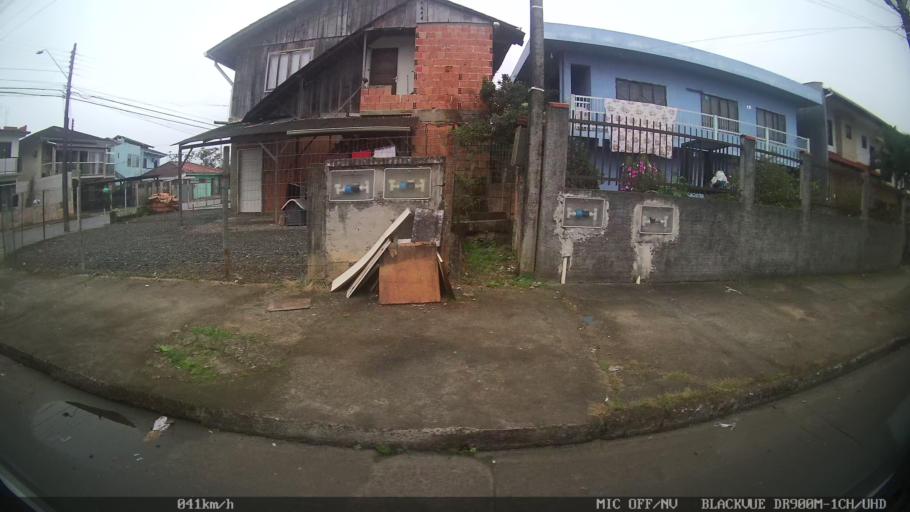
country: BR
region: Santa Catarina
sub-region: Joinville
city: Joinville
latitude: -26.2822
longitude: -48.7985
